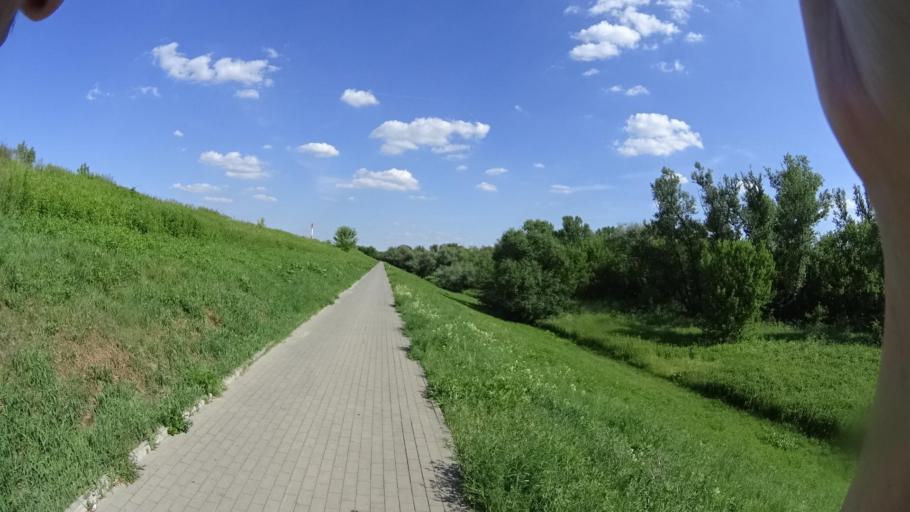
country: PL
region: Masovian Voivodeship
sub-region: Warszawa
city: Bialoleka
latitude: 52.3057
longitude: 20.9589
